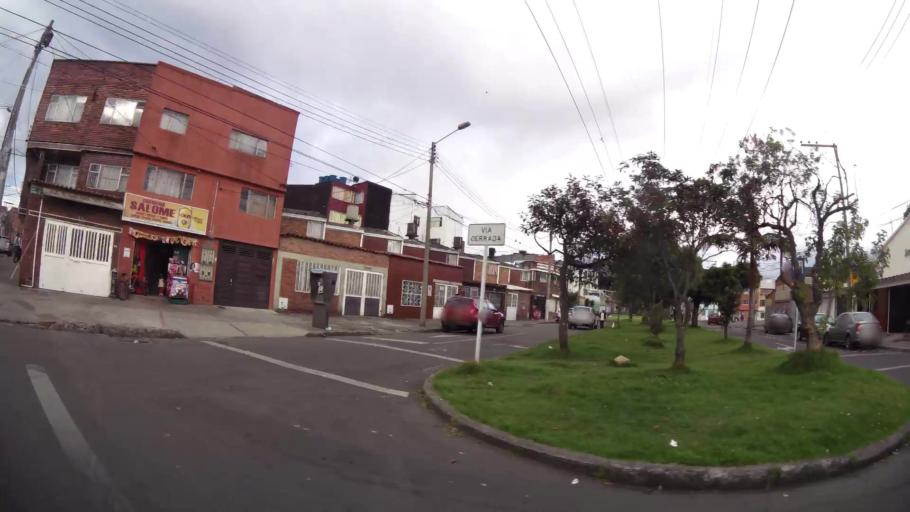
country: CO
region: Bogota D.C.
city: Bogota
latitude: 4.6104
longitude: -74.1113
